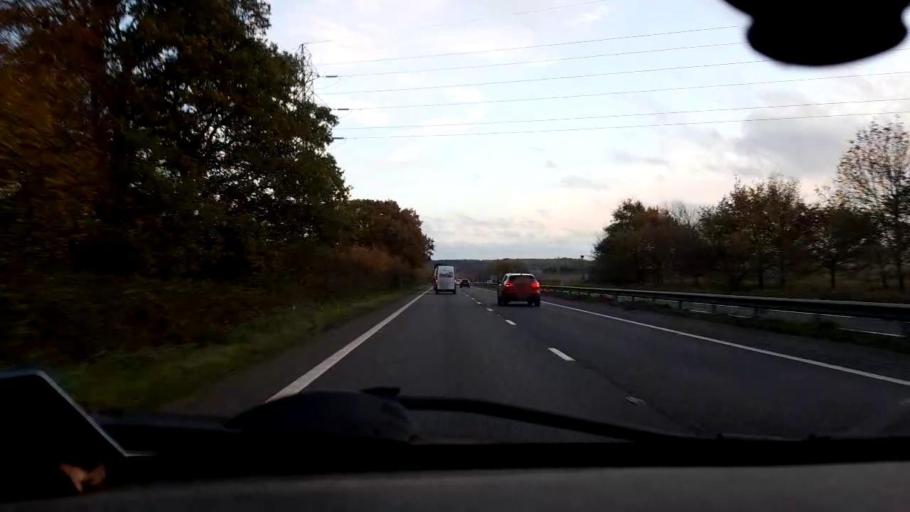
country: GB
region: England
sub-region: Norfolk
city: Costessey
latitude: 52.6422
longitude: 1.1924
